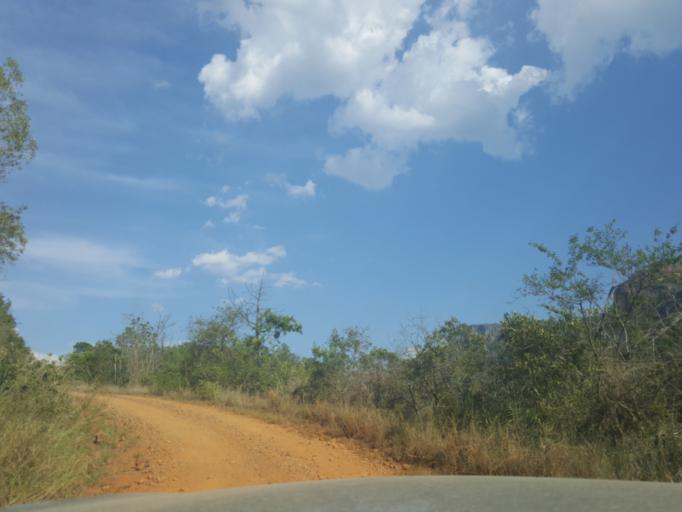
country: ZA
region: Limpopo
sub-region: Mopani District Municipality
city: Hoedspruit
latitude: -24.5929
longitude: 30.8334
